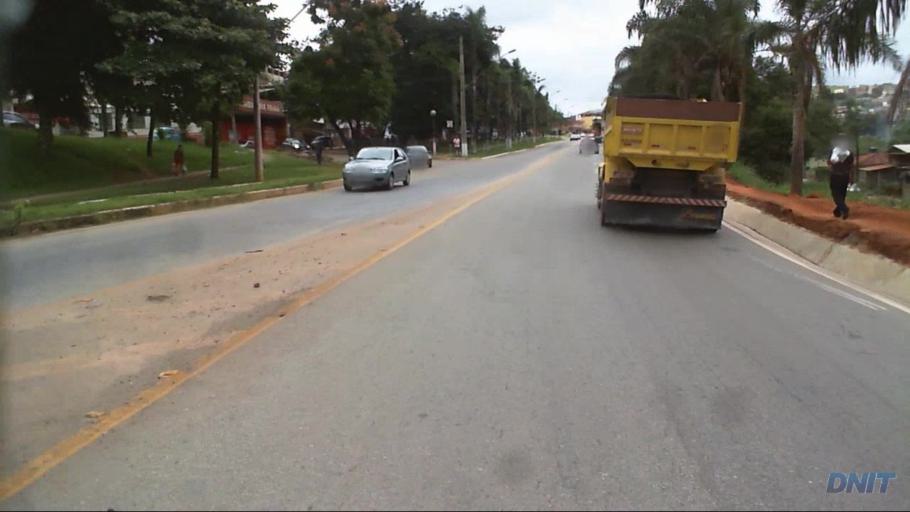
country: BR
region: Minas Gerais
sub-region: Joao Monlevade
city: Joao Monlevade
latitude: -19.8389
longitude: -43.1823
